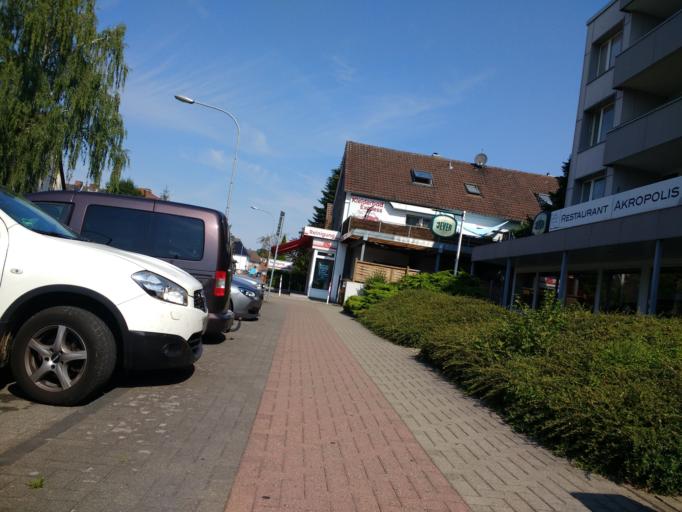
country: DE
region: Lower Saxony
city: Gifhorn
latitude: 52.4738
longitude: 10.5458
